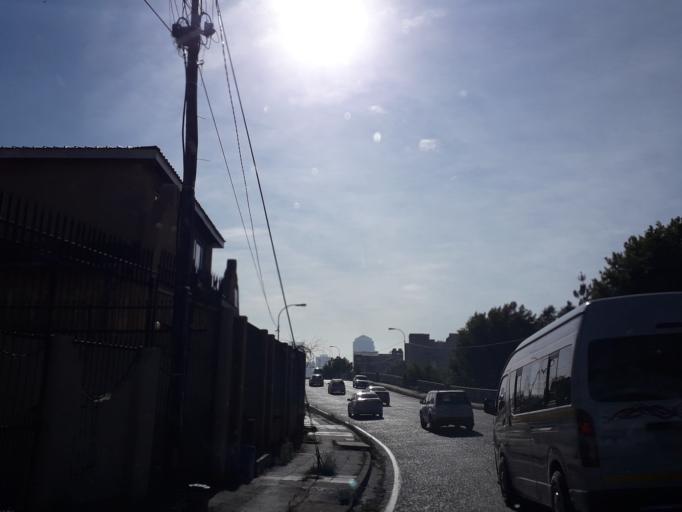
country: ZA
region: Gauteng
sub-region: City of Johannesburg Metropolitan Municipality
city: Johannesburg
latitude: -26.2017
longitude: 28.0172
